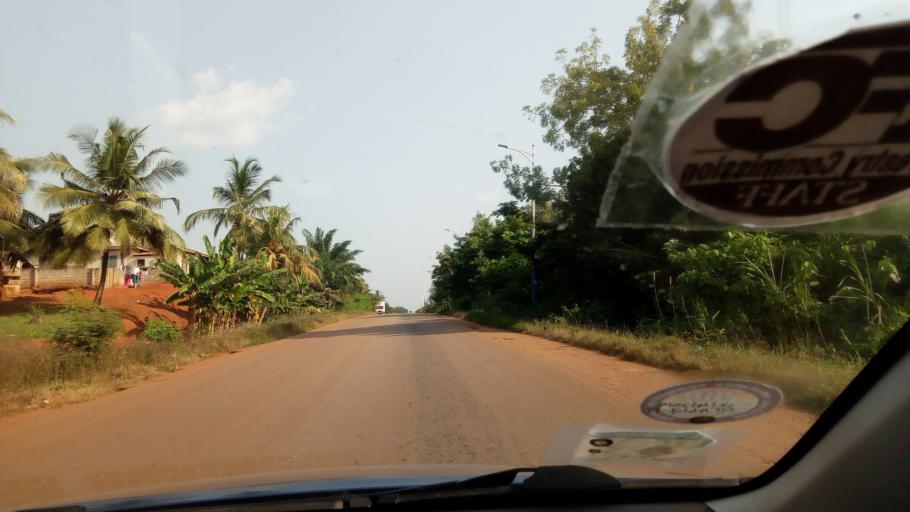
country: GH
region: Western
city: Bibiani
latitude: 6.8065
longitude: -2.5271
